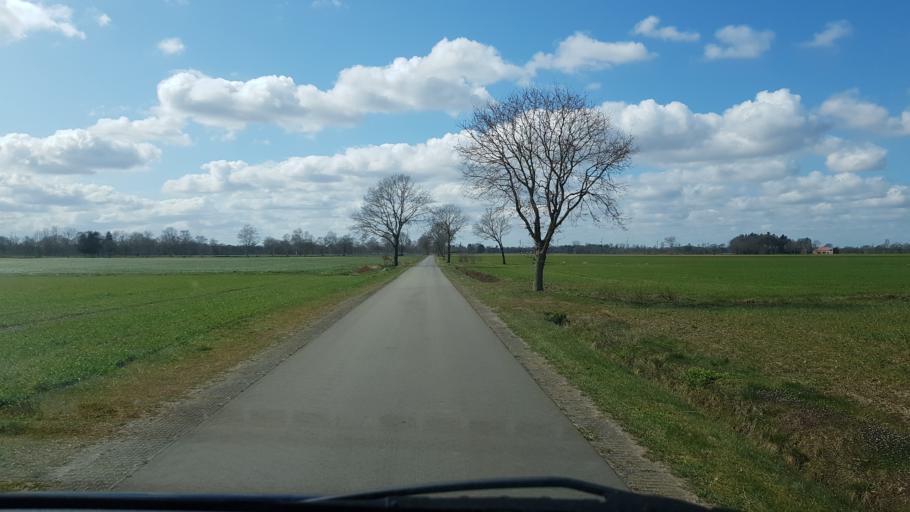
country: DE
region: Lower Saxony
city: Bad Zwischenahn
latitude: 53.1759
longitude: 7.9233
